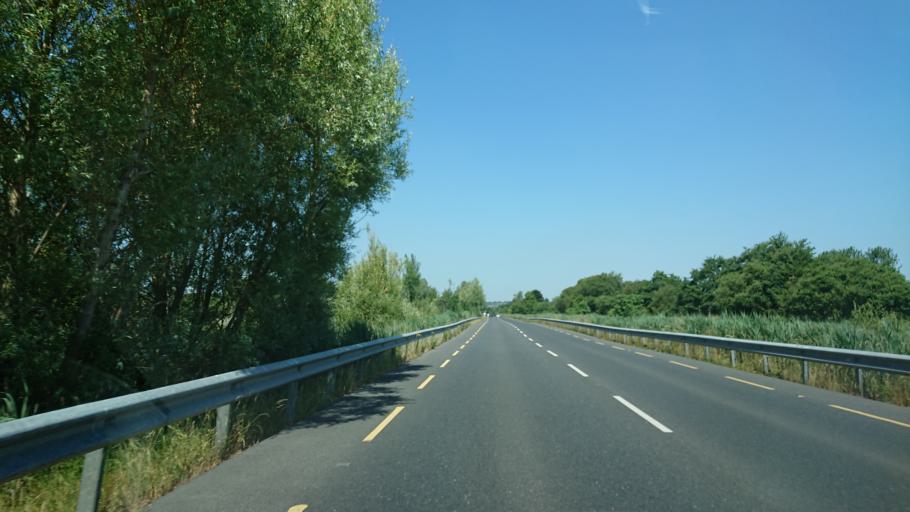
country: IE
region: Munster
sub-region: Waterford
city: Waterford
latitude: 52.2339
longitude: -7.1215
